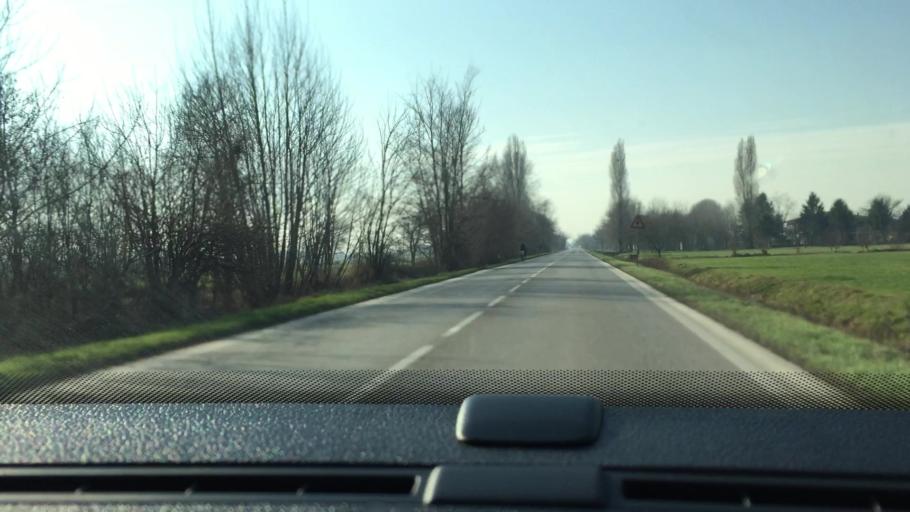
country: IT
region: Lombardy
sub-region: Provincia di Mantova
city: Goito
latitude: 45.2412
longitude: 10.6491
